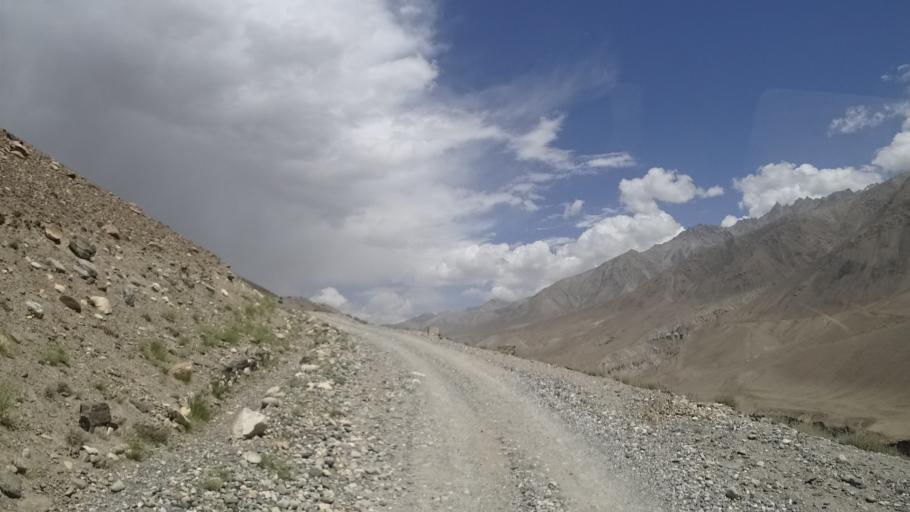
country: AF
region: Badakhshan
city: Khandud
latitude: 37.0843
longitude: 72.7002
